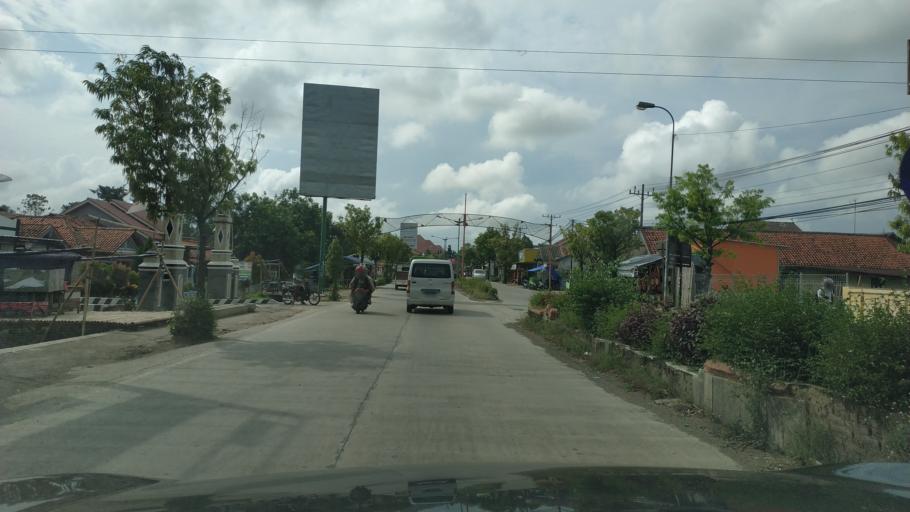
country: ID
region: Central Java
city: Pemalang
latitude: -6.9146
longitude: 109.3827
